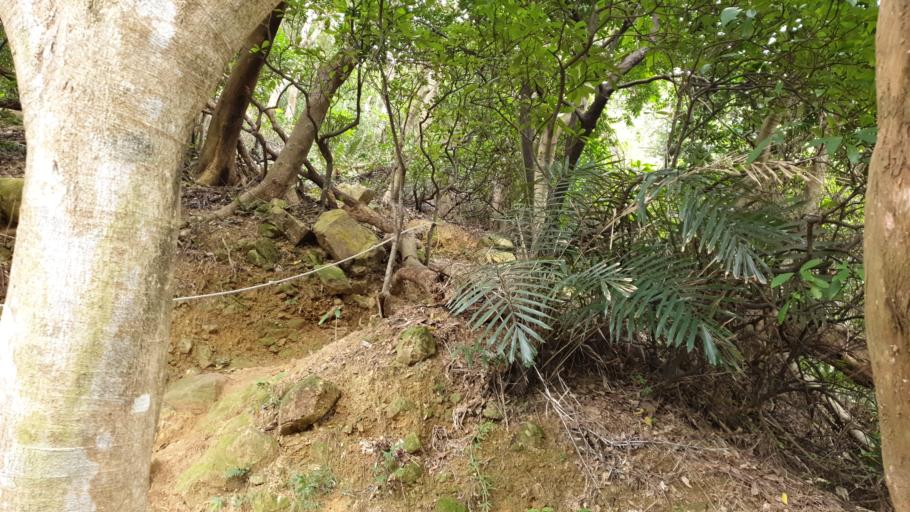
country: TW
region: Taipei
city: Taipei
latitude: 25.0921
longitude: 121.5462
